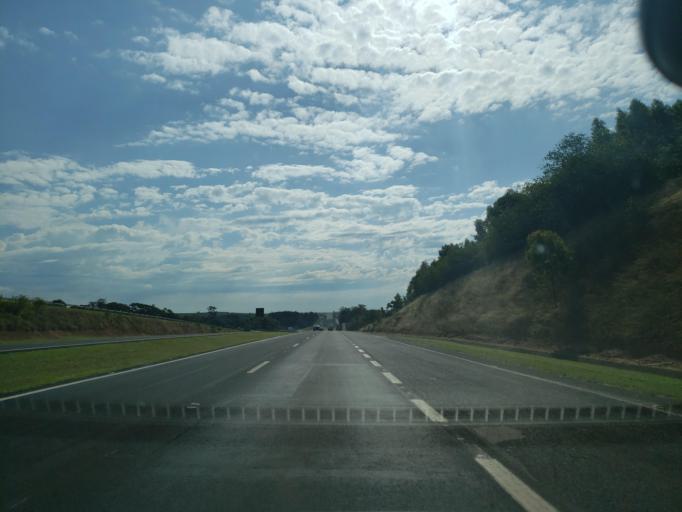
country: BR
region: Sao Paulo
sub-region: Pirajui
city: Pirajui
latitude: -21.9907
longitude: -49.4397
